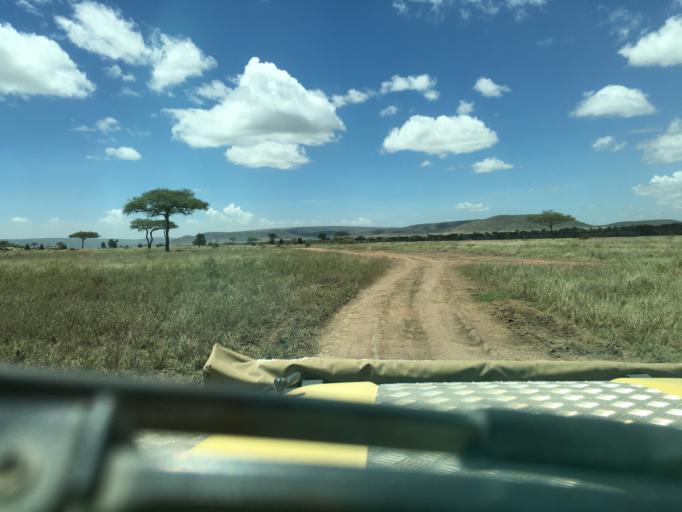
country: TZ
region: Simiyu
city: Kisesa
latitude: -2.7087
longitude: 34.7631
